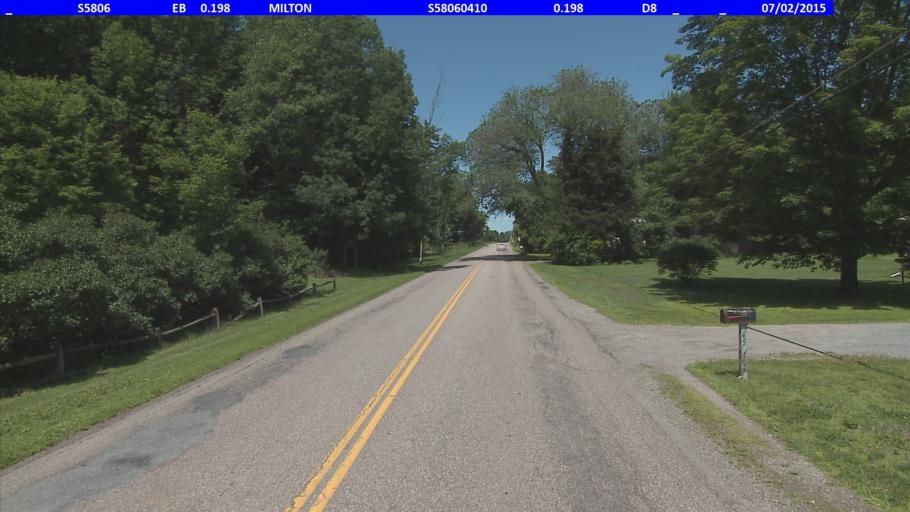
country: US
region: Vermont
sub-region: Chittenden County
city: Milton
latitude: 44.6540
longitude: -73.1172
